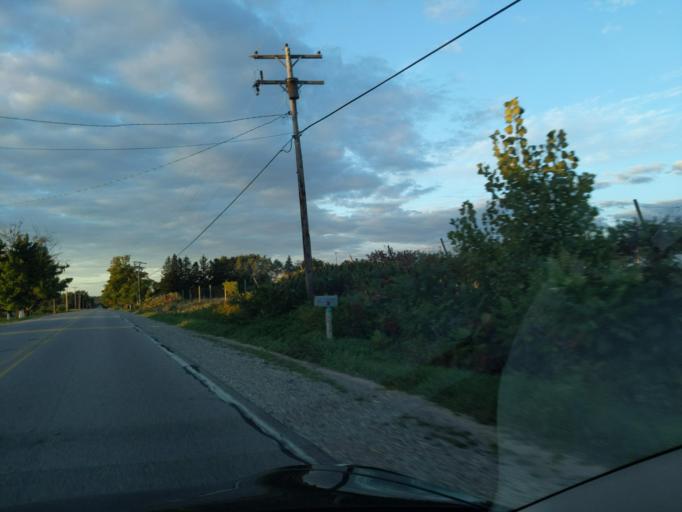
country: US
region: Michigan
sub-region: Antrim County
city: Elk Rapids
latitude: 44.8371
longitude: -85.4052
